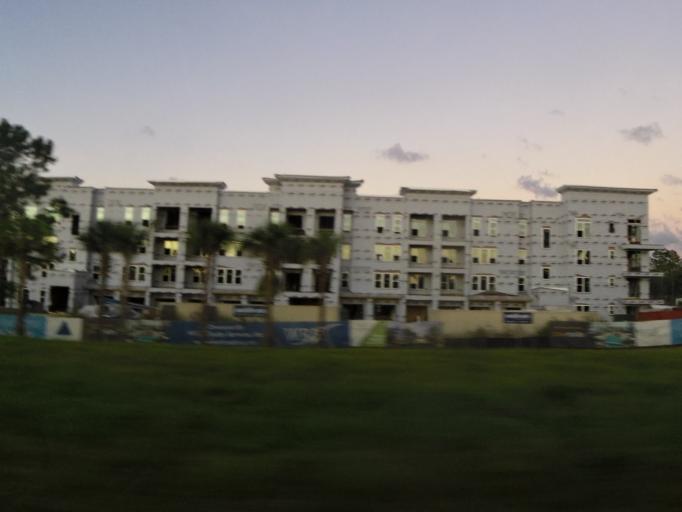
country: US
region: Florida
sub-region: Duval County
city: Jacksonville
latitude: 30.2509
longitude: -81.5499
